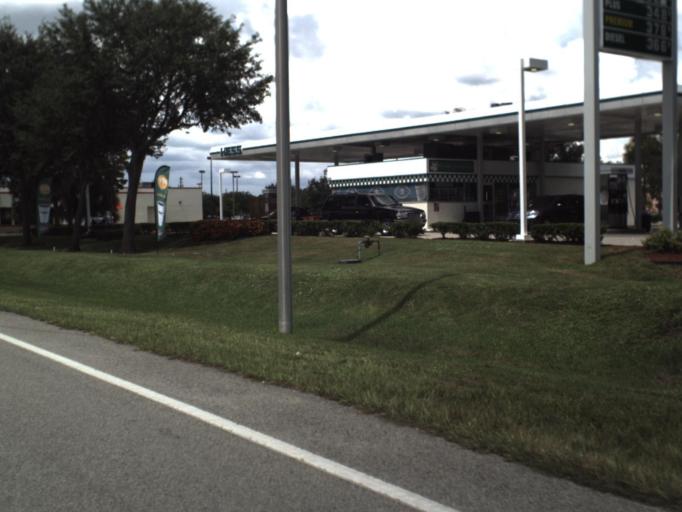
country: US
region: Florida
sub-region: Charlotte County
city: Port Charlotte
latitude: 27.0115
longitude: -82.1427
